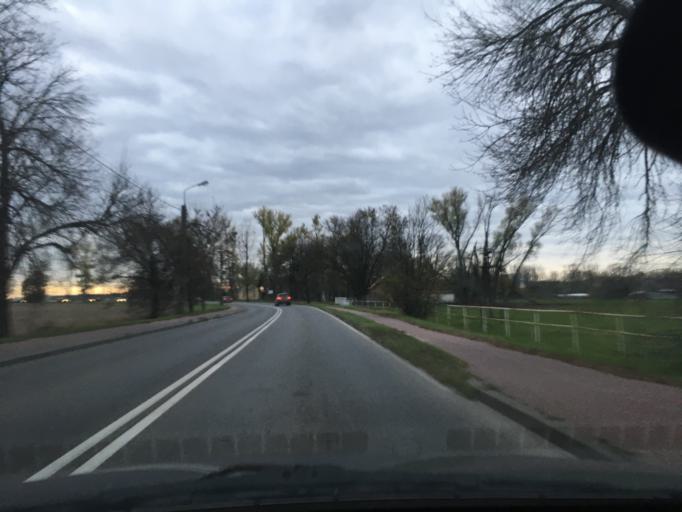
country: PL
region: Masovian Voivodeship
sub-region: Powiat piaseczynski
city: Lesznowola
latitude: 52.0896
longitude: 20.9356
